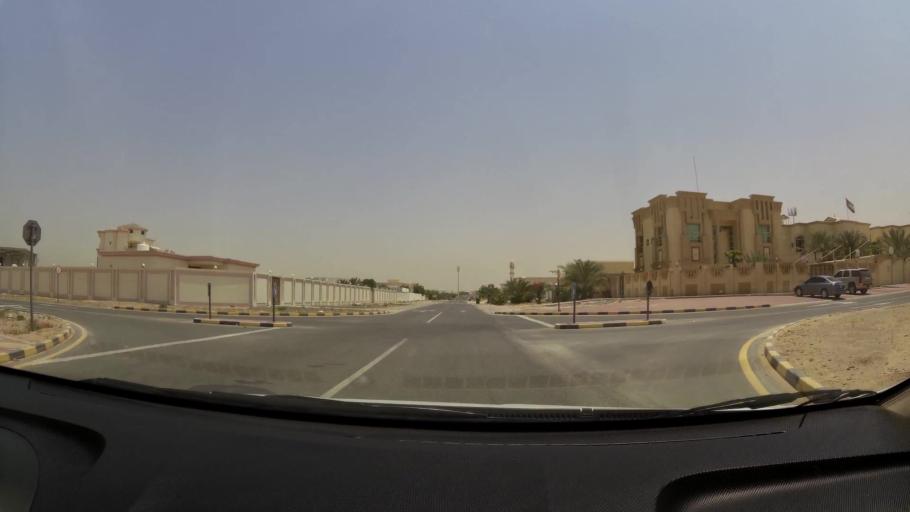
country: AE
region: Ajman
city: Ajman
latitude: 25.4066
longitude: 55.5207
